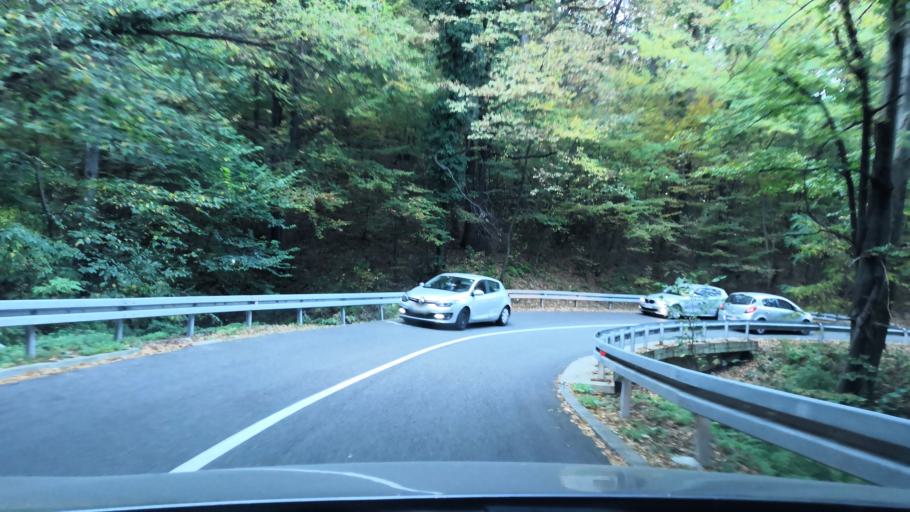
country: RS
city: Vrdnik
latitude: 45.1605
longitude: 19.7753
